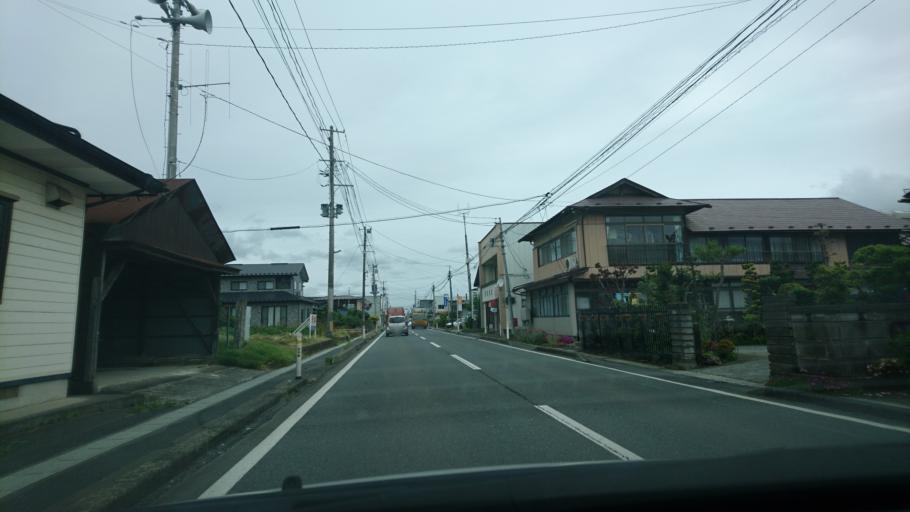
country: JP
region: Iwate
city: Ichinoseki
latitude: 38.9545
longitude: 141.1299
